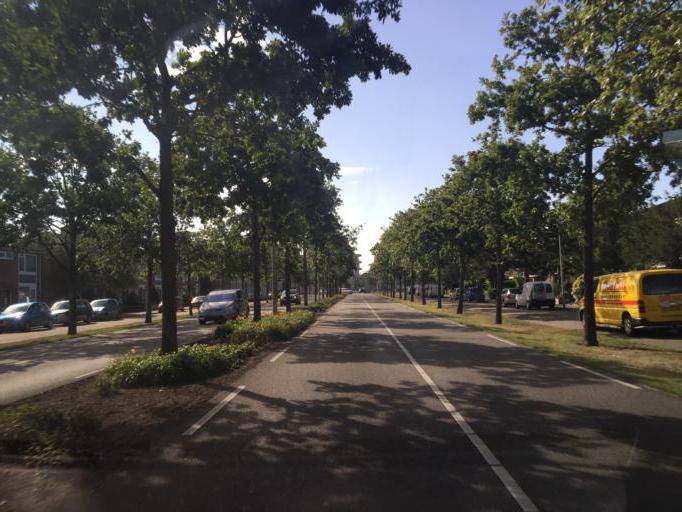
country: NL
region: South Holland
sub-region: Gemeente Noordwijk
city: Noordwijk-Binnen
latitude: 52.2403
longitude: 4.4490
